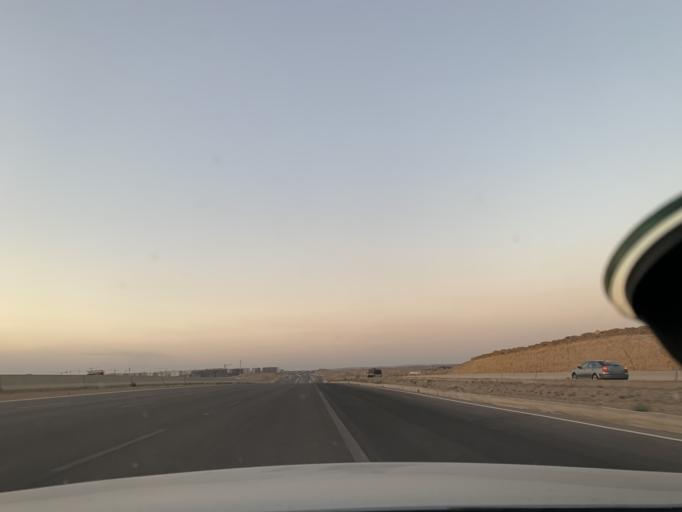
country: EG
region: Muhafazat al Qahirah
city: Halwan
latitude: 29.9538
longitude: 31.5407
